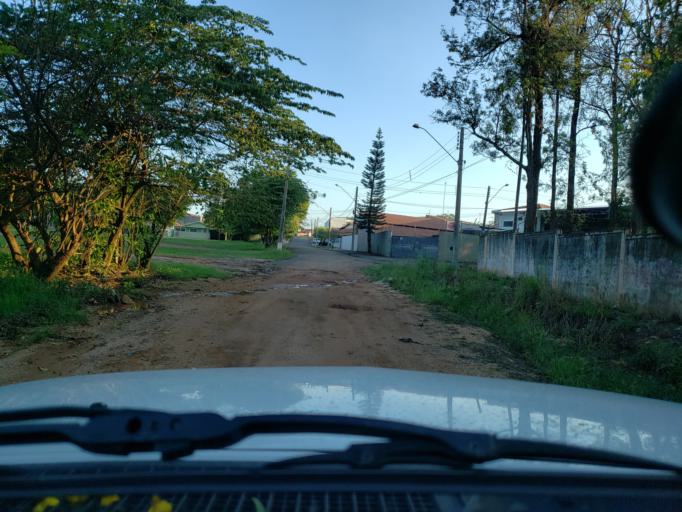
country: BR
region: Sao Paulo
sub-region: Moji-Guacu
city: Mogi-Gaucu
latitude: -22.3397
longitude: -46.9389
